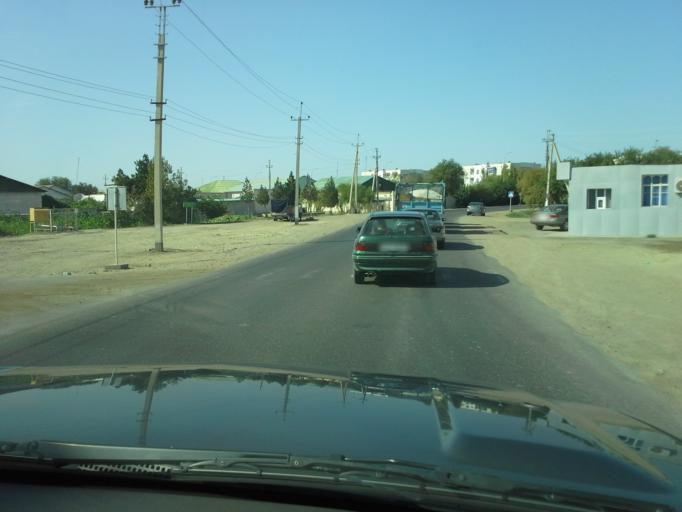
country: TM
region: Dasoguz
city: Dasoguz
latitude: 41.8251
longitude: 59.9535
